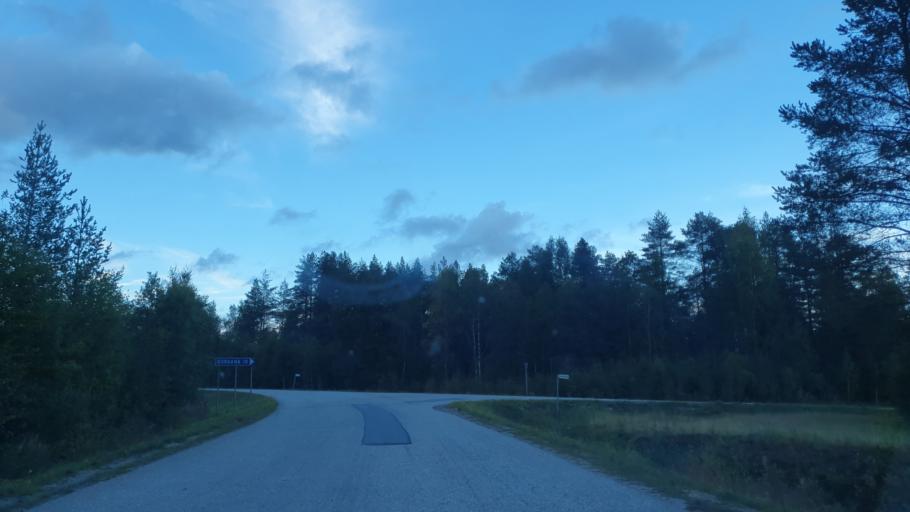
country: FI
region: Kainuu
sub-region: Kehys-Kainuu
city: Kuhmo
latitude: 64.3836
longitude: 29.8702
